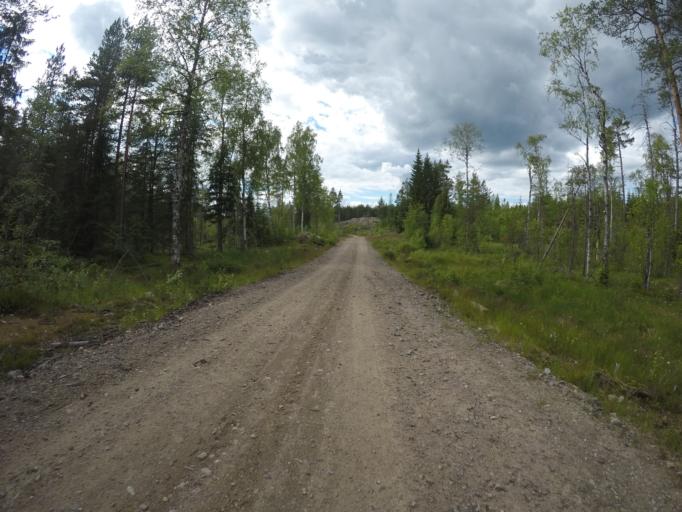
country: SE
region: Vaermland
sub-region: Filipstads Kommun
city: Lesjofors
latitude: 60.0811
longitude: 14.4343
